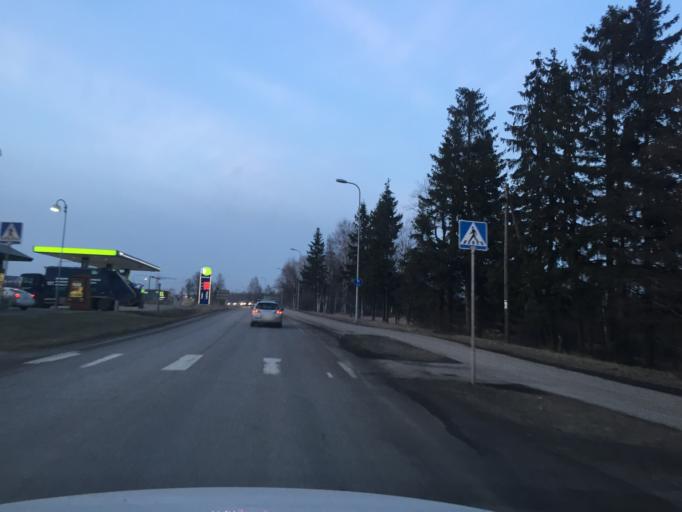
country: FI
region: Uusimaa
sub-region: Helsinki
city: Vantaa
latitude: 60.2706
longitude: 24.9750
